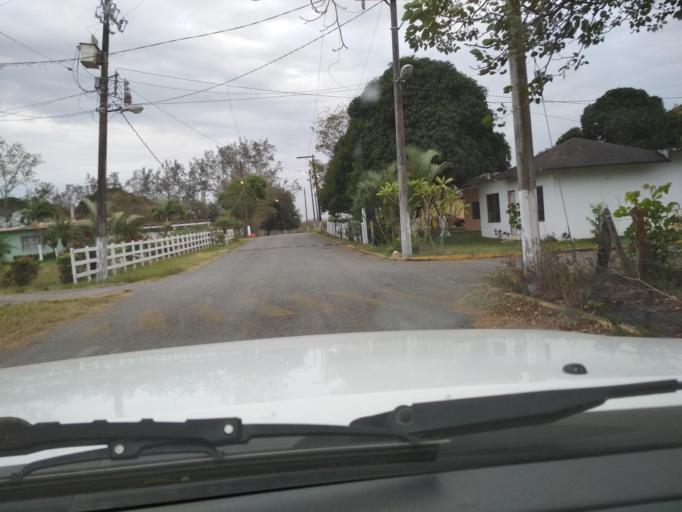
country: MX
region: Veracruz
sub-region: Veracruz
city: Delfino Victoria (Santa Fe)
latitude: 19.1593
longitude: -96.2940
